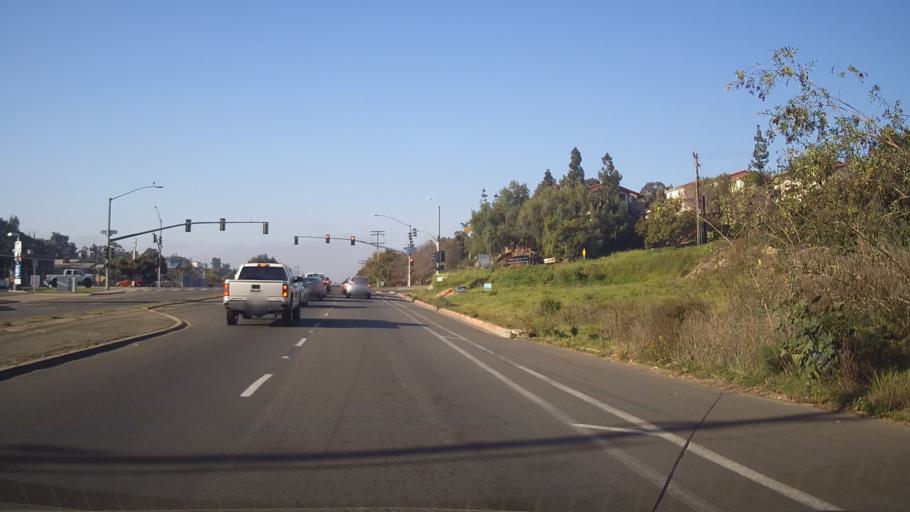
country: US
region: California
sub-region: San Diego County
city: National City
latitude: 32.7295
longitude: -117.0991
